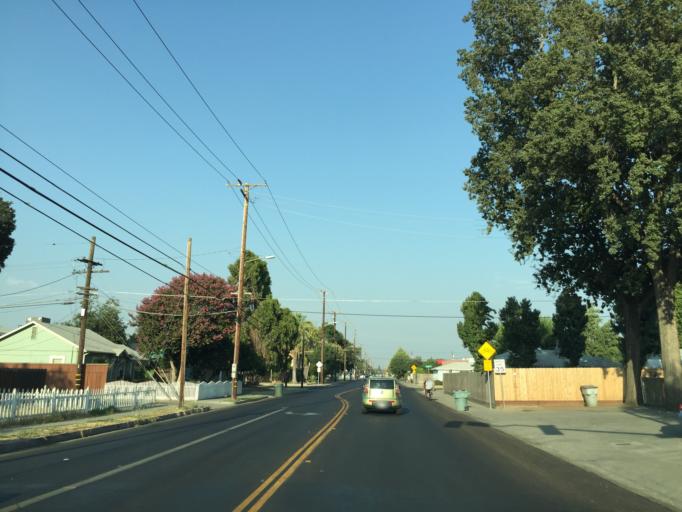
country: US
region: California
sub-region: Tulare County
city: Visalia
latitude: 36.3201
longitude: -119.2921
